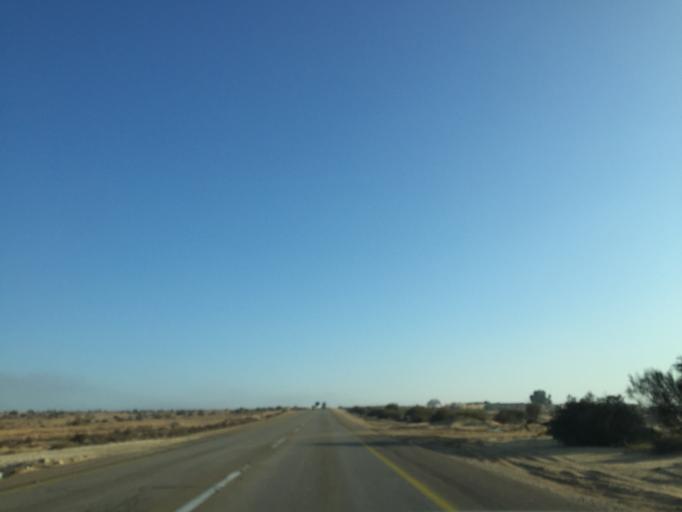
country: IL
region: Southern District
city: Yeroham
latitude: 31.0088
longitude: 34.9533
